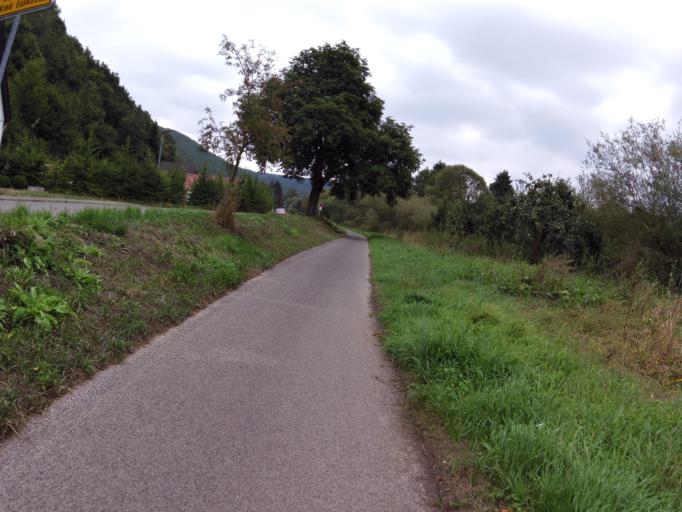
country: DE
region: North Rhine-Westphalia
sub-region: Regierungsbezirk Koln
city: Schleiden
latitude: 50.5781
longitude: 6.4785
